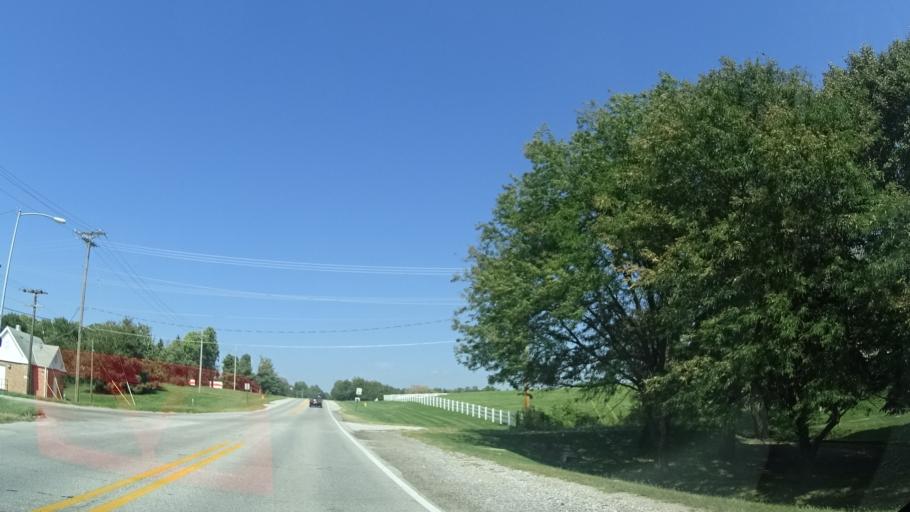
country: US
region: Nebraska
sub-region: Sarpy County
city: Offutt Air Force Base
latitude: 41.1288
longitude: -95.9474
